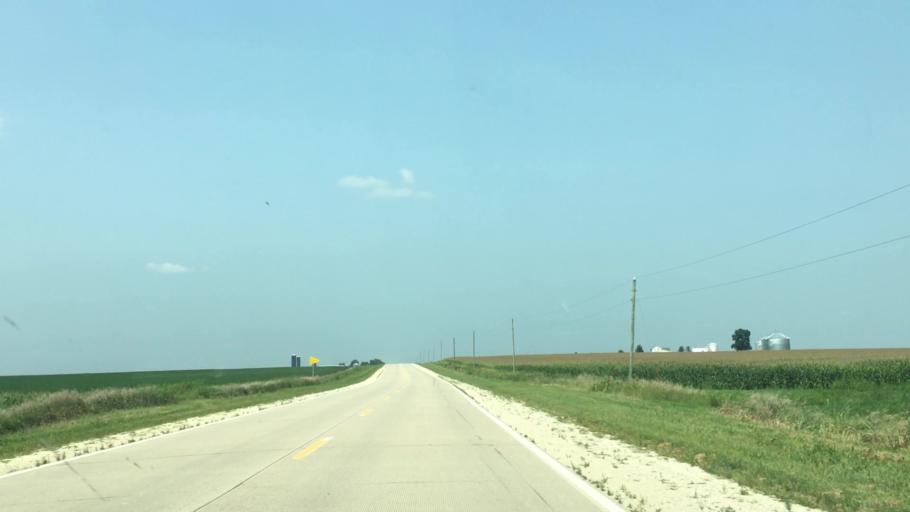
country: US
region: Iowa
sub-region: Fayette County
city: Fayette
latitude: 42.7300
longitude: -91.8041
